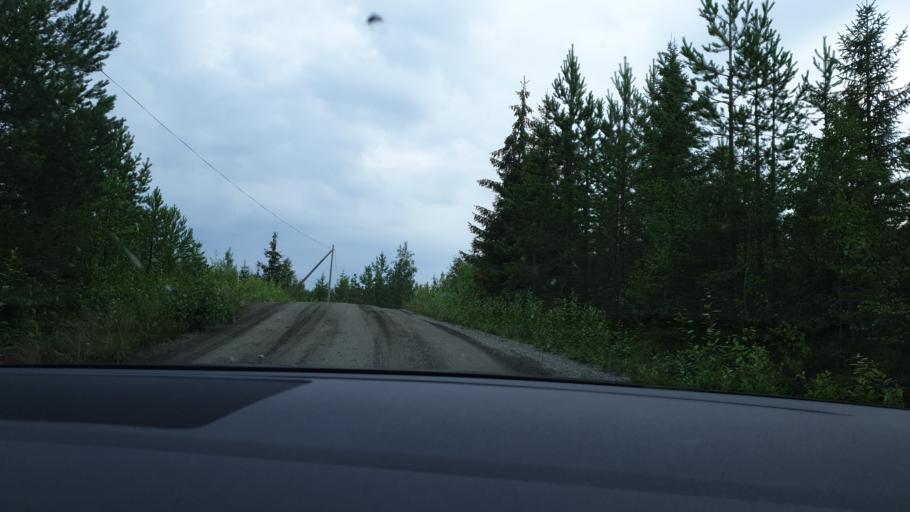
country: SE
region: Gaevleborg
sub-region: Hudiksvalls Kommun
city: Iggesund
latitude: 61.5272
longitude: 17.0128
